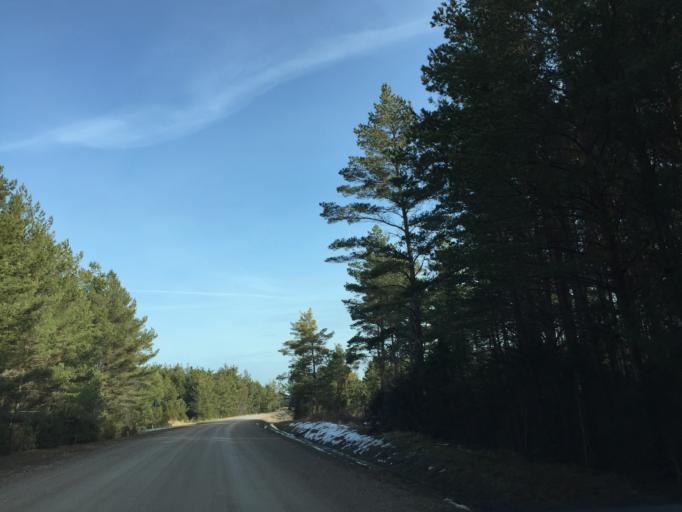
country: EE
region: Saare
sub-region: Kuressaare linn
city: Kuressaare
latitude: 58.2806
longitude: 21.9179
